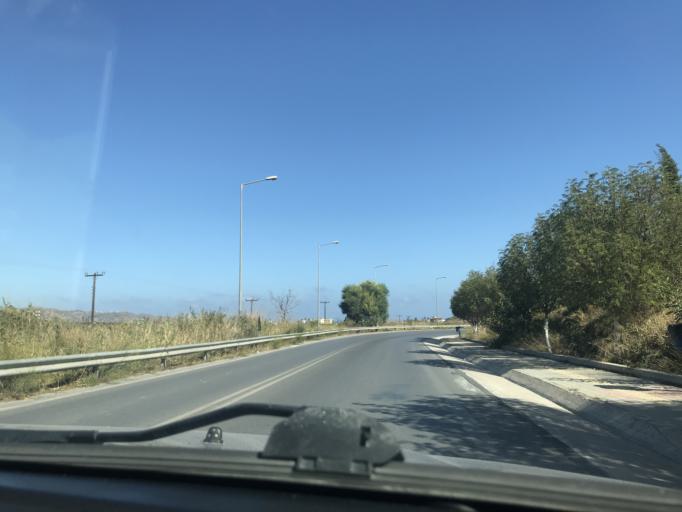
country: GR
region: Crete
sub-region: Nomos Irakleiou
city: Gazi
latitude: 35.3246
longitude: 25.0622
